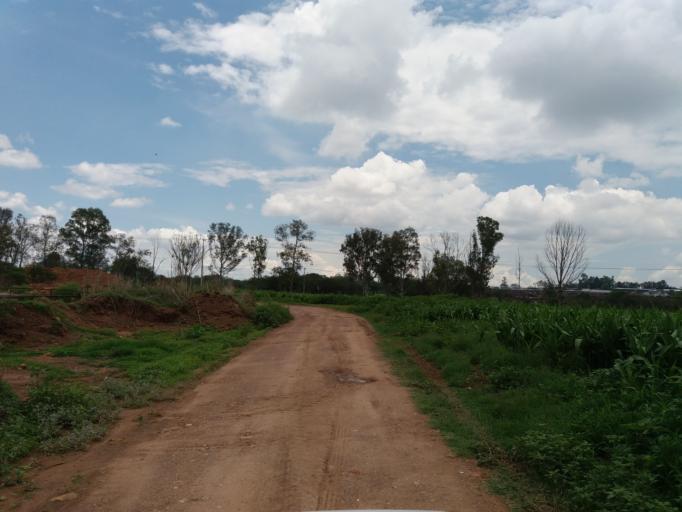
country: MX
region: Aguascalientes
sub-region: Aguascalientes
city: La Loma de los Negritos
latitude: 21.8318
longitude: -102.3314
